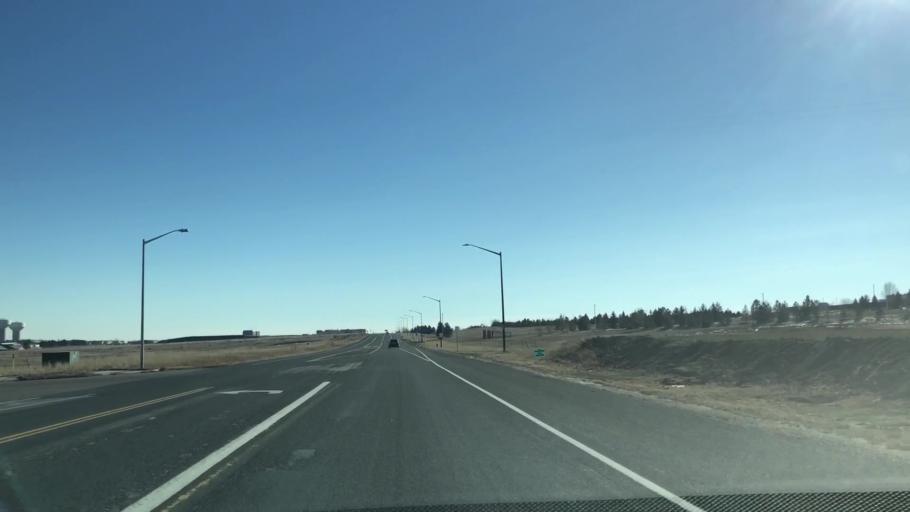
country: US
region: Colorado
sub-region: Weld County
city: Windsor
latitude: 40.4506
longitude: -104.9824
